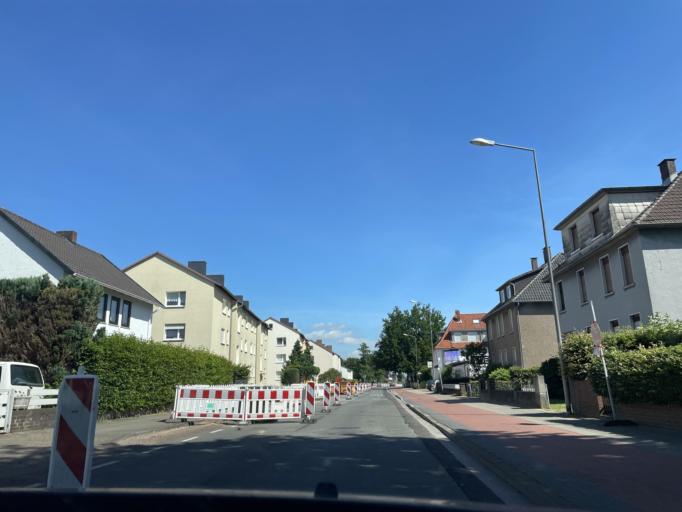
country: DE
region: North Rhine-Westphalia
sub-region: Regierungsbezirk Detmold
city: Minden
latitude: 52.3047
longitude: 8.9114
